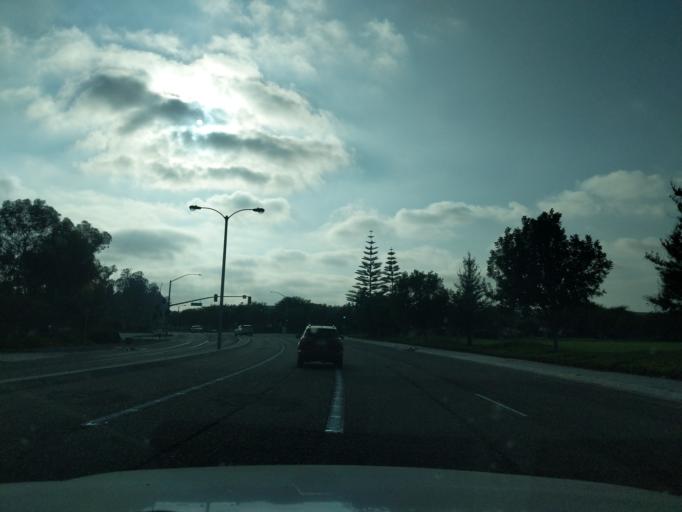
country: US
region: California
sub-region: Ventura County
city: Camarillo
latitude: 34.2166
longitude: -119.0209
